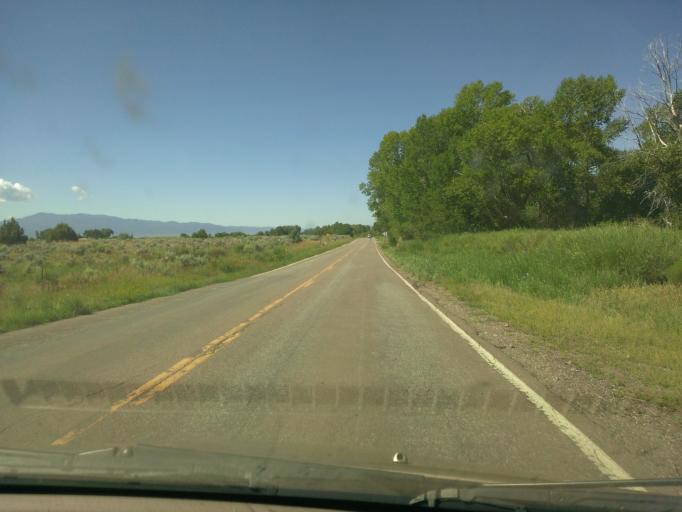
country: US
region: New Mexico
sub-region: Taos County
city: Arroyo Seco
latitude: 36.5081
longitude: -105.5845
